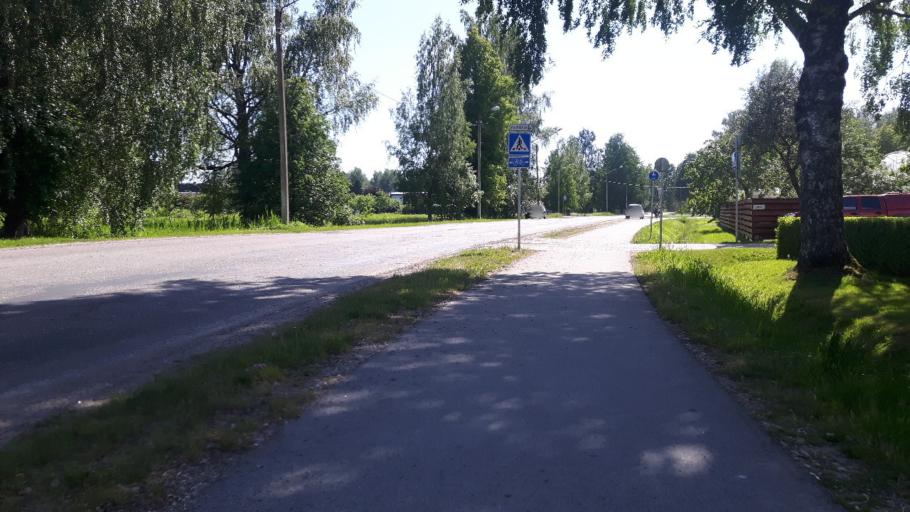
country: EE
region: Paernumaa
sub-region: Paikuse vald
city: Paikuse
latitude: 58.3990
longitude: 24.6450
